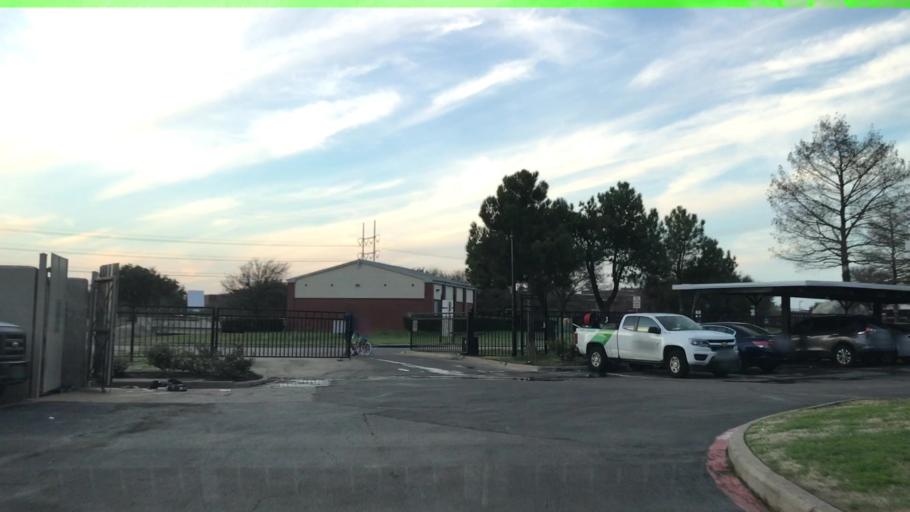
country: US
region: Texas
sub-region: Dallas County
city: Coppell
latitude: 32.9094
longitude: -96.9873
